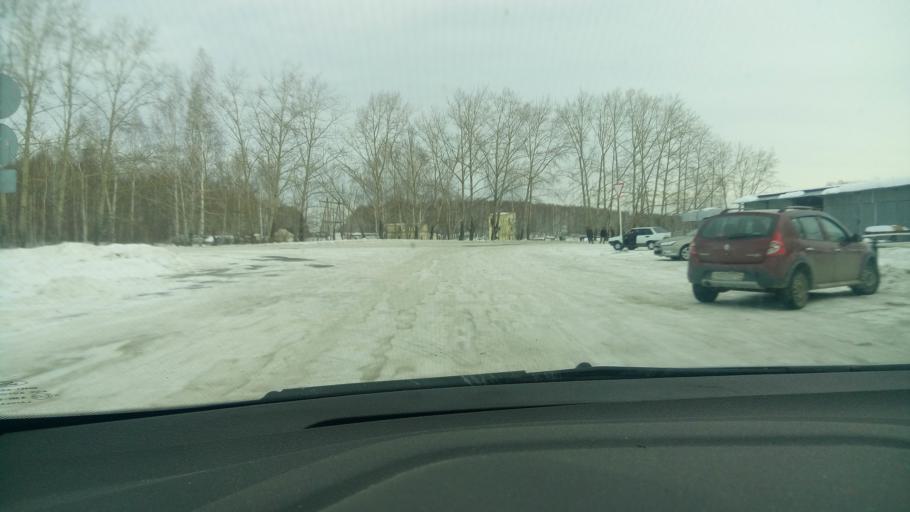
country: RU
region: Chelyabinsk
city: Ozersk
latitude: 55.7741
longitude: 60.7519
